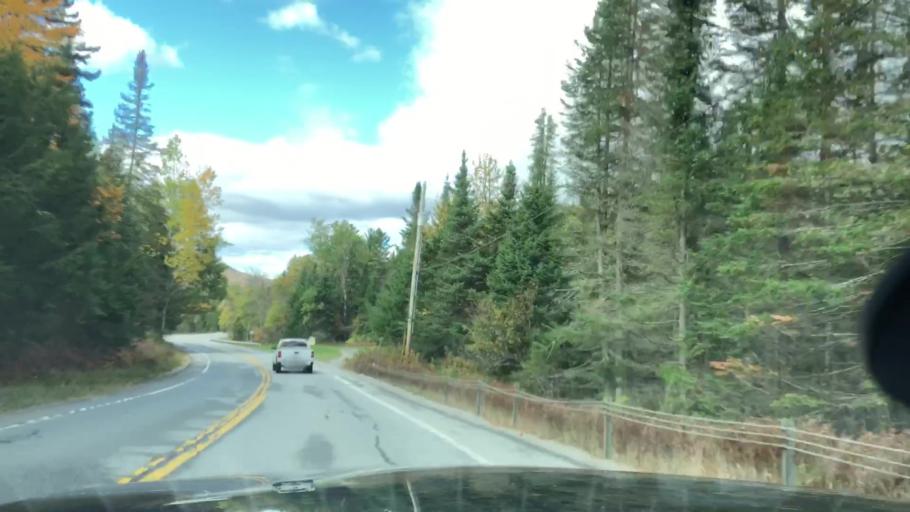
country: US
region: New York
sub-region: Essex County
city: Lake Placid
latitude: 43.8705
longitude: -74.0003
